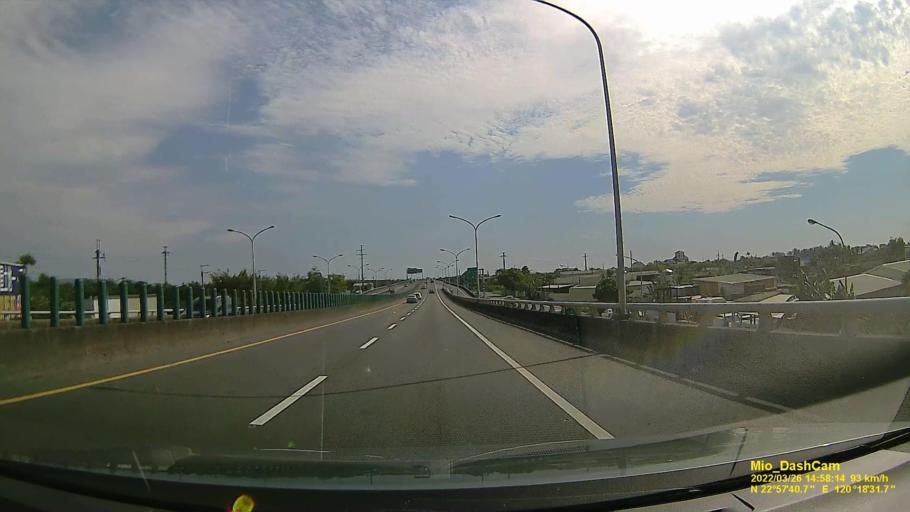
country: TW
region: Taiwan
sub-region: Tainan
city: Tainan
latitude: 22.9611
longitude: 120.3086
